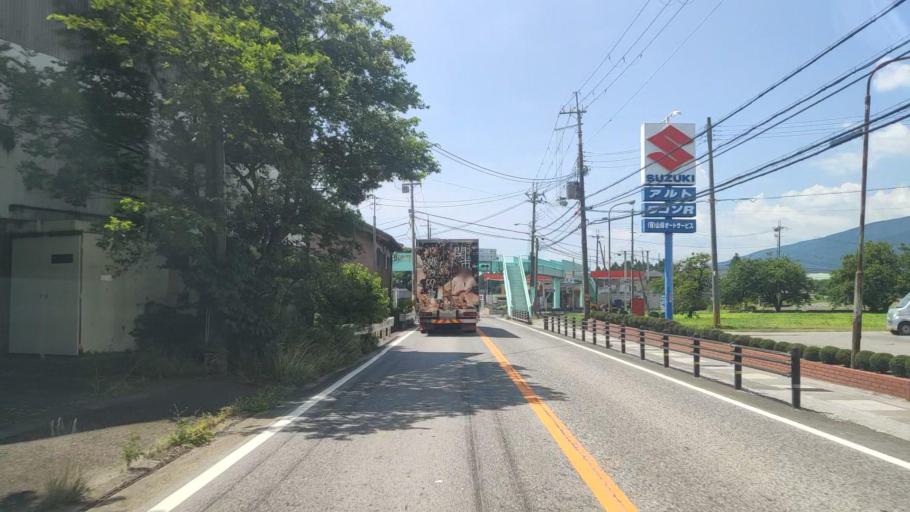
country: JP
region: Shiga Prefecture
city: Nagahama
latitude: 35.3770
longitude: 136.3807
